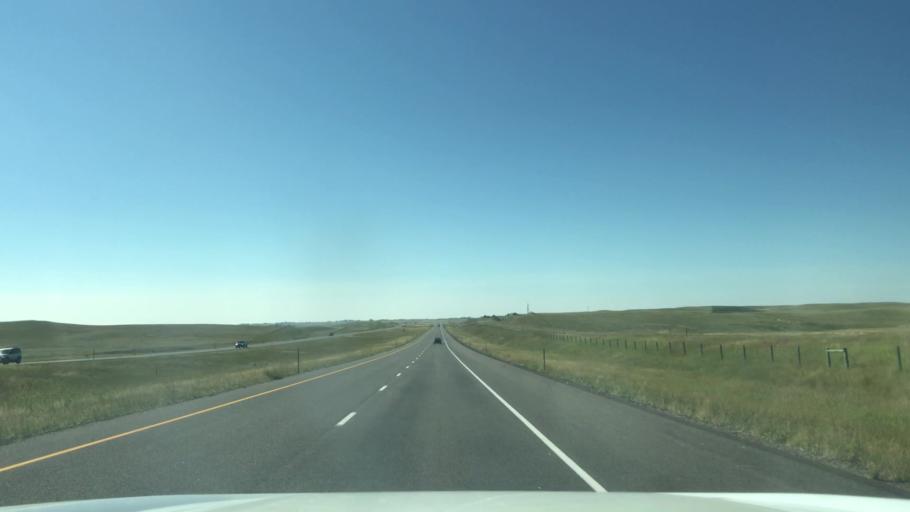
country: US
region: Wyoming
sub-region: Laramie County
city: Ranchettes
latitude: 41.2713
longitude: -104.8447
